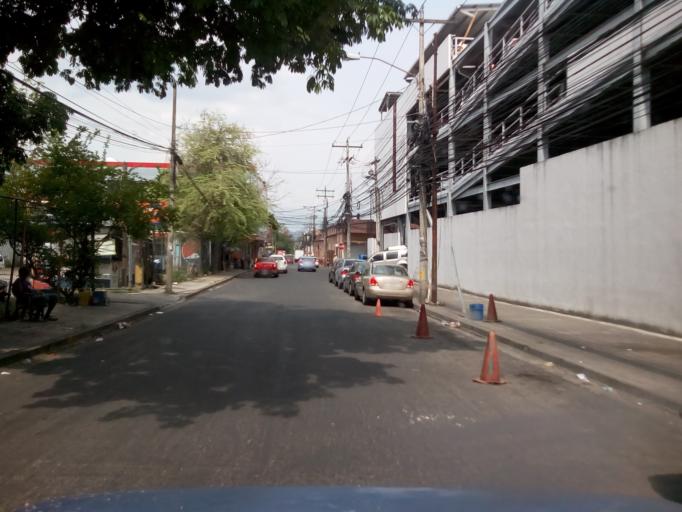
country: HN
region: Cortes
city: San Pedro Sula
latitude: 15.5067
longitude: -88.0250
